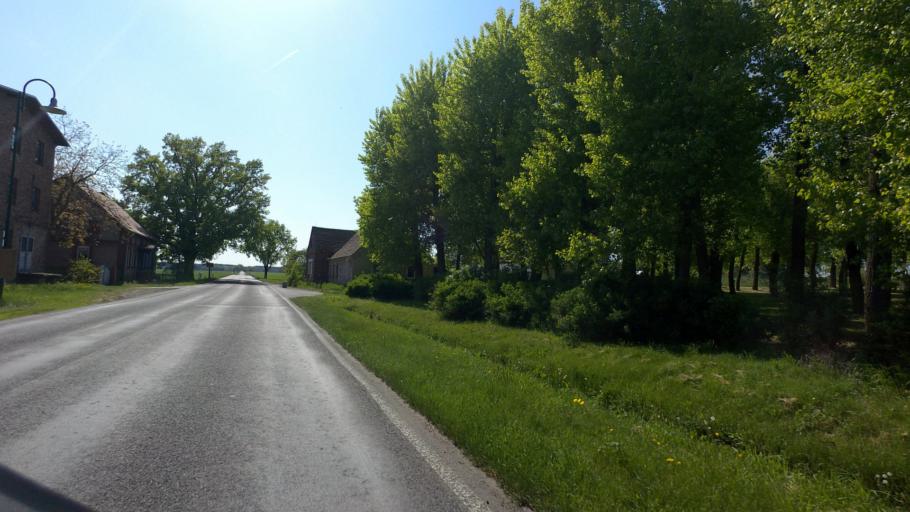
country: DE
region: Brandenburg
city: Tauche
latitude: 52.0622
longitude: 14.1423
